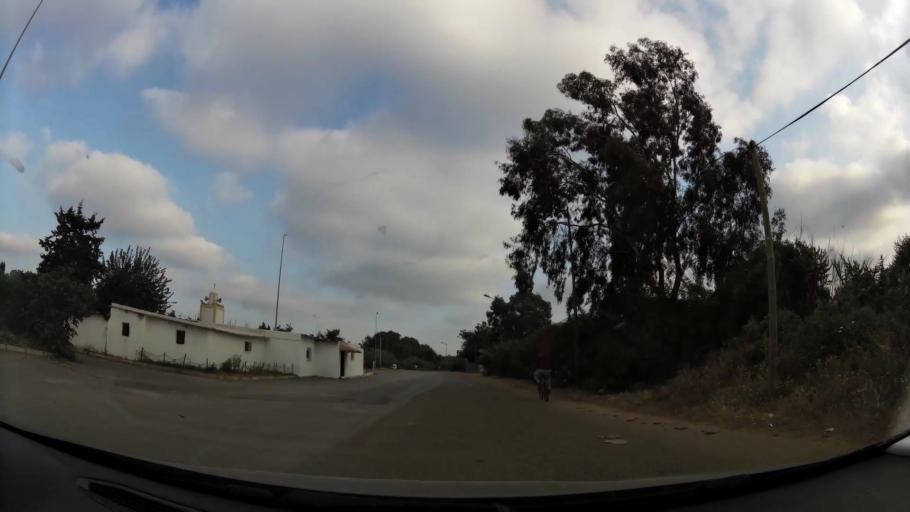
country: MA
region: Rabat-Sale-Zemmour-Zaer
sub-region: Skhirate-Temara
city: Temara
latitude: 33.9480
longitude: -6.8482
